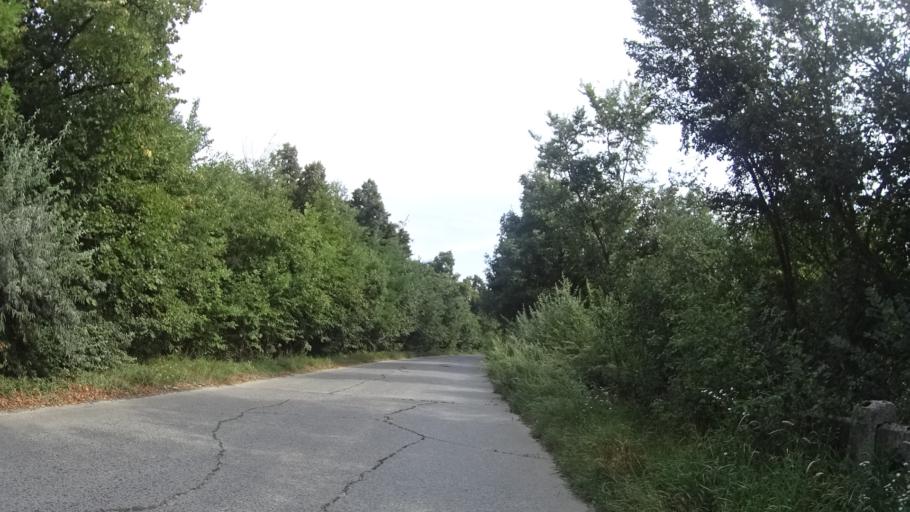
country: HU
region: Fejer
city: Polgardi
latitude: 47.0798
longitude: 18.3202
